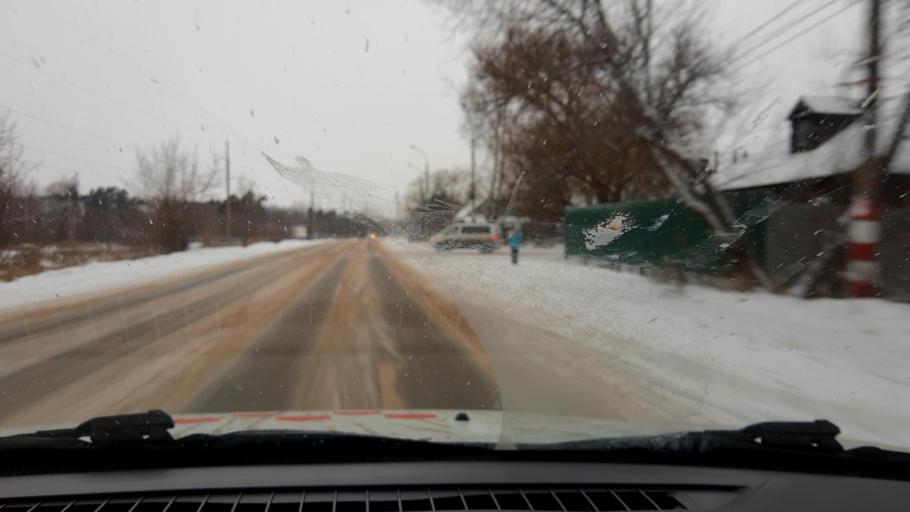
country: RU
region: Nizjnij Novgorod
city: Bor
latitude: 56.3296
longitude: 44.1224
